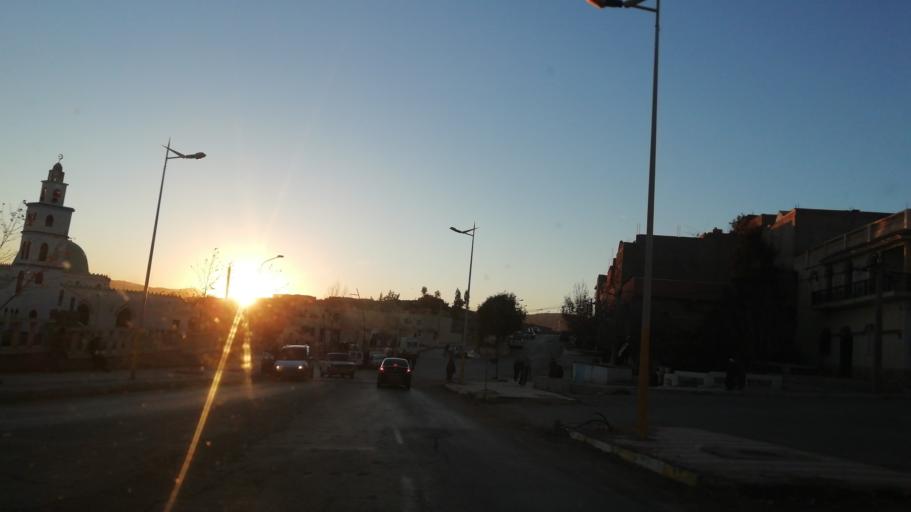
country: DZ
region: Saida
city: Saida
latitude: 34.8344
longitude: 0.1691
